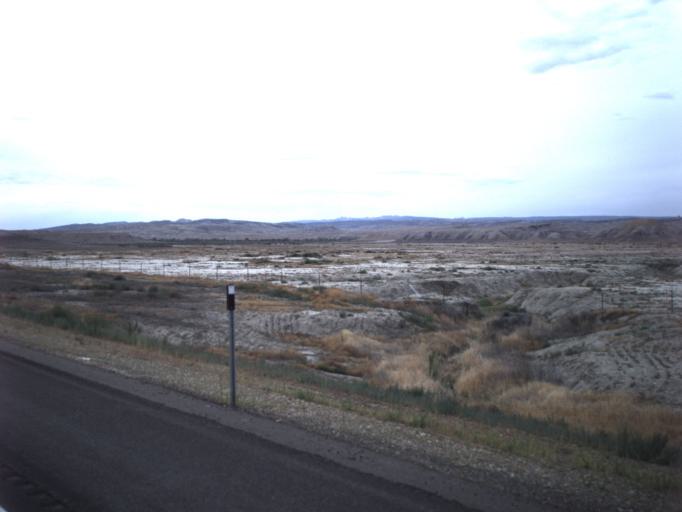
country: US
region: Utah
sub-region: Carbon County
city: East Carbon City
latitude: 39.3240
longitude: -110.3661
